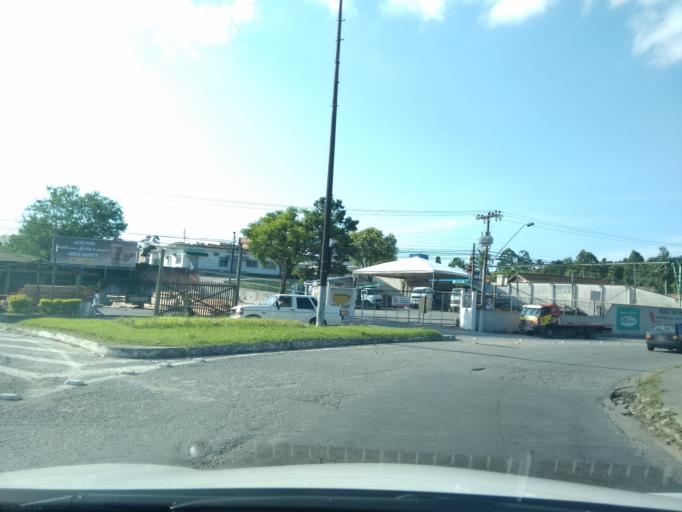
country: BR
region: Santa Catarina
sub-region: Blumenau
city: Blumenau
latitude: -26.8707
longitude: -49.0928
